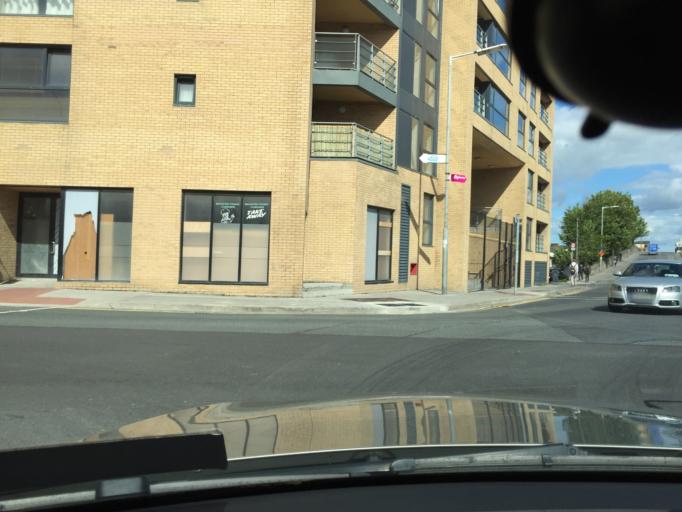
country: IE
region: Leinster
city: Ringsend
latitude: 53.3501
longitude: -6.2351
